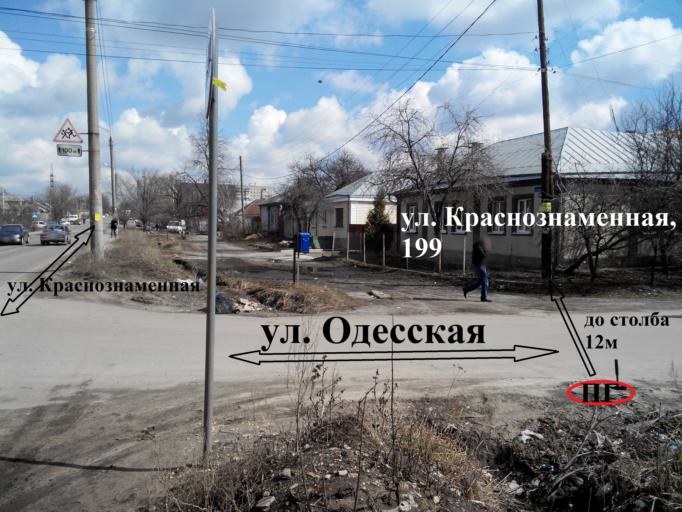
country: RU
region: Voronezj
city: Voronezh
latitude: 51.6330
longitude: 39.1690
